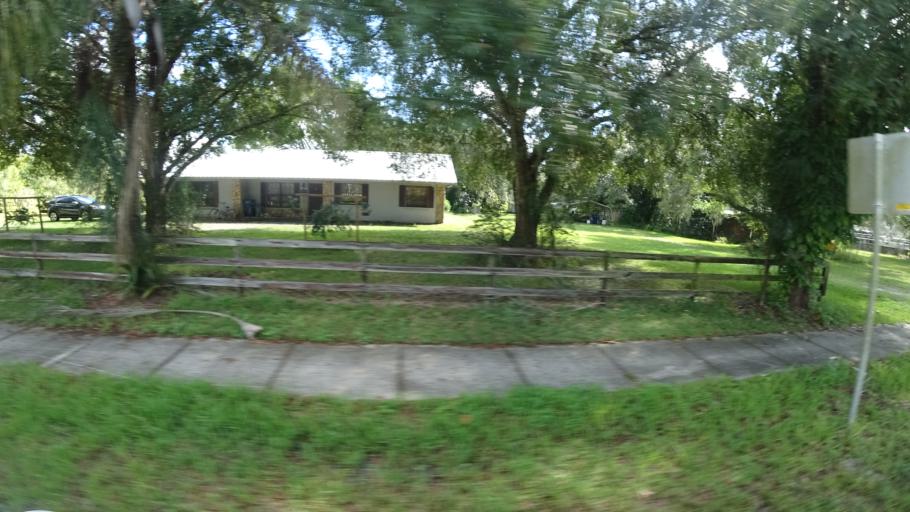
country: US
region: Florida
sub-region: Sarasota County
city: Lake Sarasota
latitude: 27.3523
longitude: -82.1625
